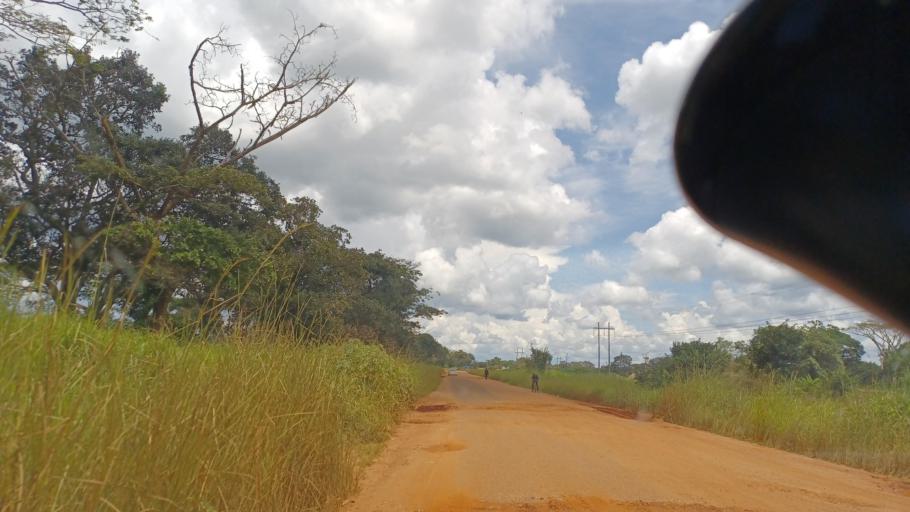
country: ZM
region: North-Western
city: Solwezi
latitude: -12.4785
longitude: 26.1985
